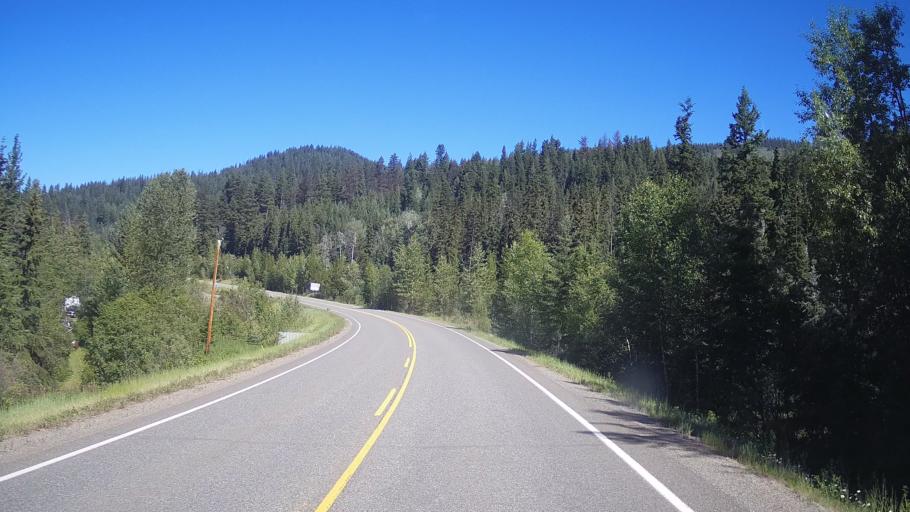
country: CA
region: British Columbia
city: Kamloops
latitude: 51.4689
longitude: -120.5331
